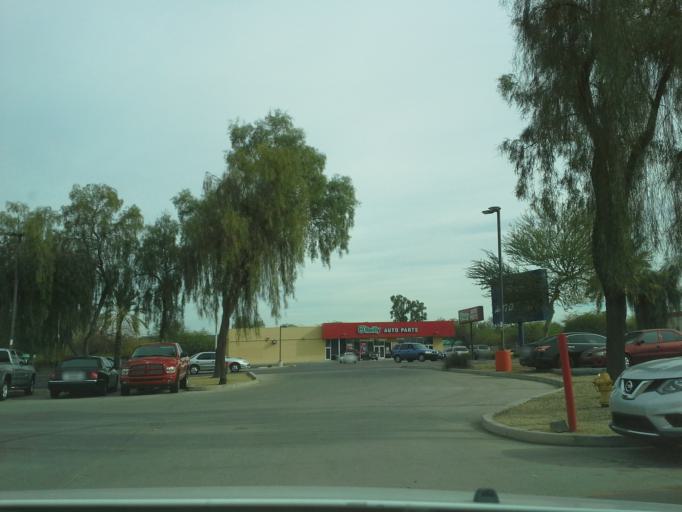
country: US
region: Arizona
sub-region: Maricopa County
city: Phoenix
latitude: 33.4021
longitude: -112.0739
